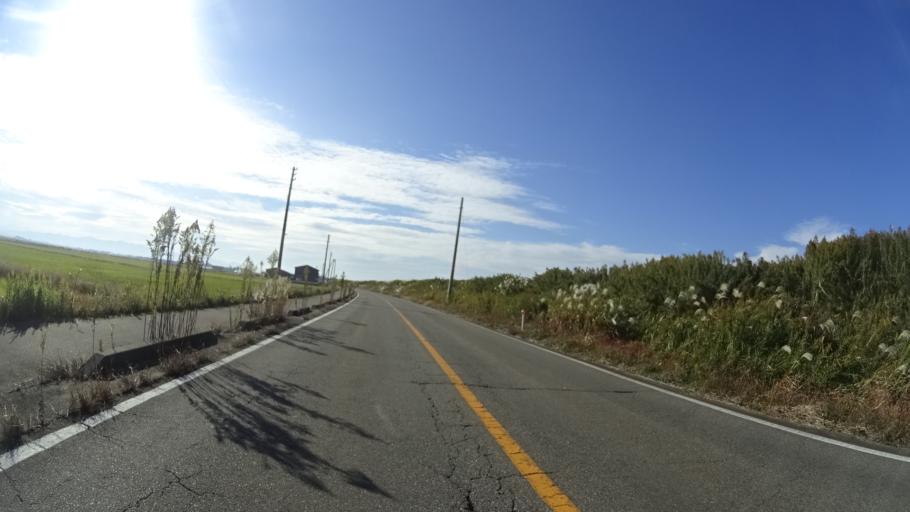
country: JP
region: Niigata
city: Yoshida-kasugacho
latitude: 37.5865
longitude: 138.8353
